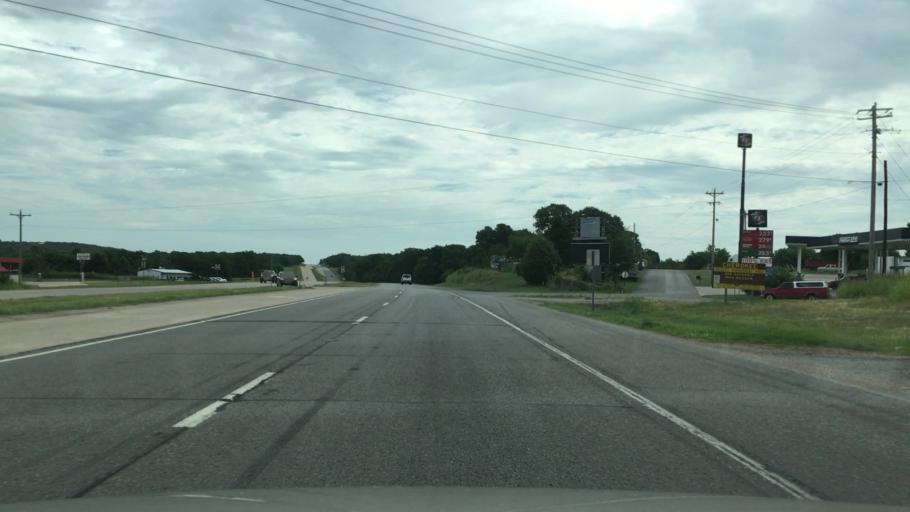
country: US
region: Oklahoma
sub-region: Cherokee County
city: Park Hill
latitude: 35.8072
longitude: -95.0747
